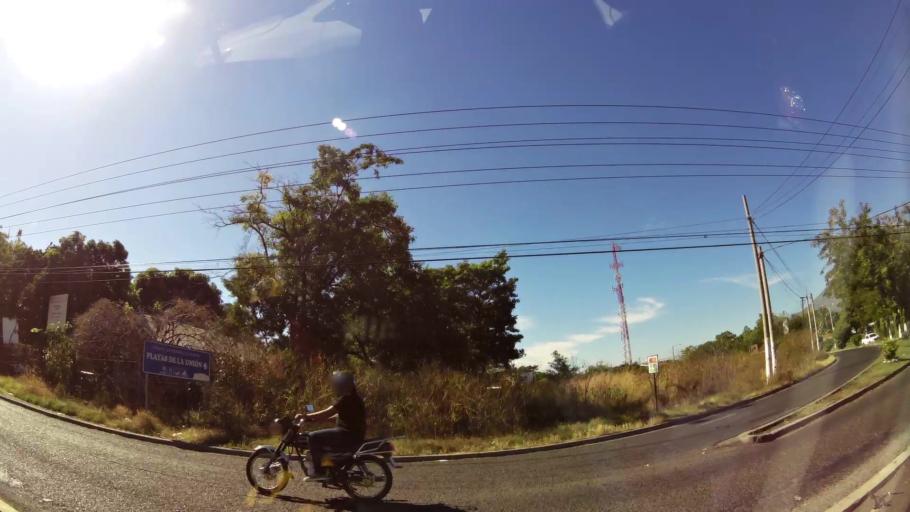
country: SV
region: San Miguel
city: San Miguel
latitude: 13.4598
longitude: -88.1593
